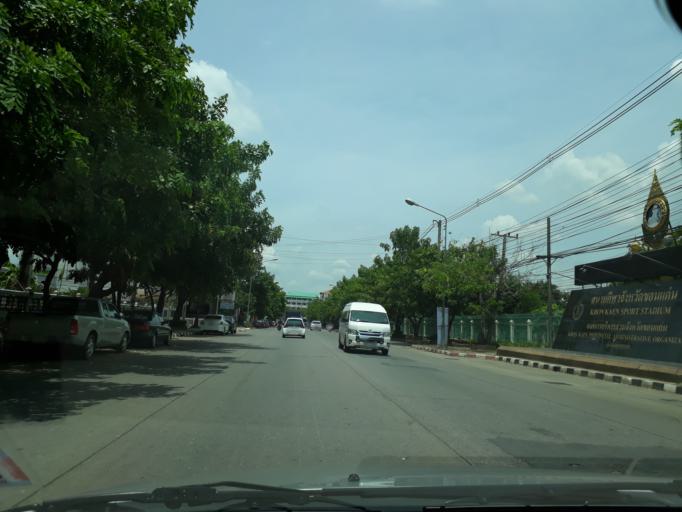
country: TH
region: Khon Kaen
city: Khon Kaen
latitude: 16.4142
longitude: 102.8279
